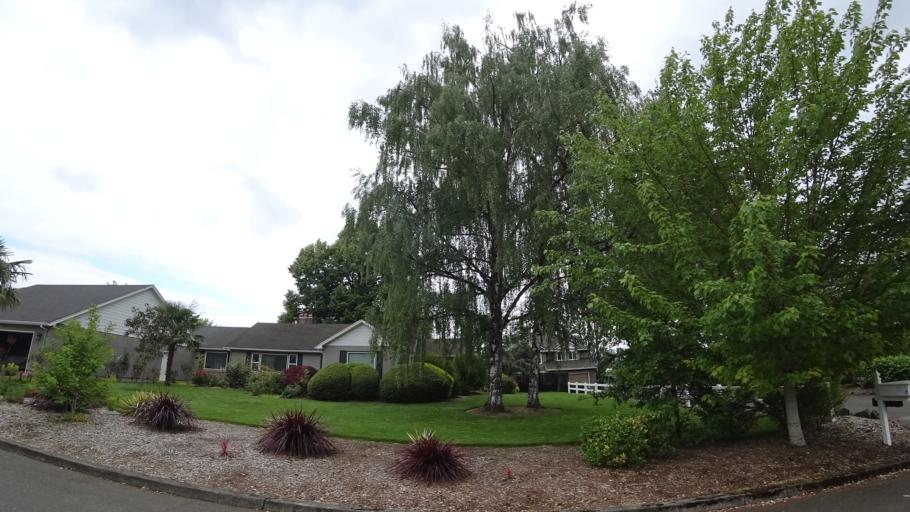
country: US
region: Oregon
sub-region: Washington County
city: Garden Home-Whitford
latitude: 45.4592
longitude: -122.7825
